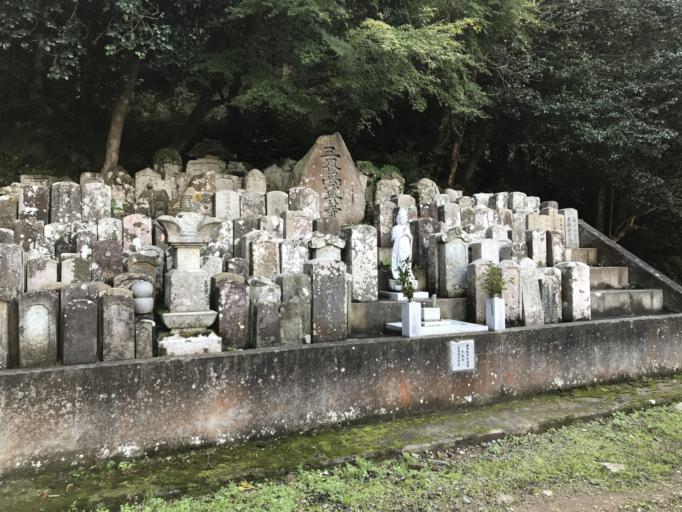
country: JP
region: Fukui
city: Obama
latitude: 35.4892
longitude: 135.7354
